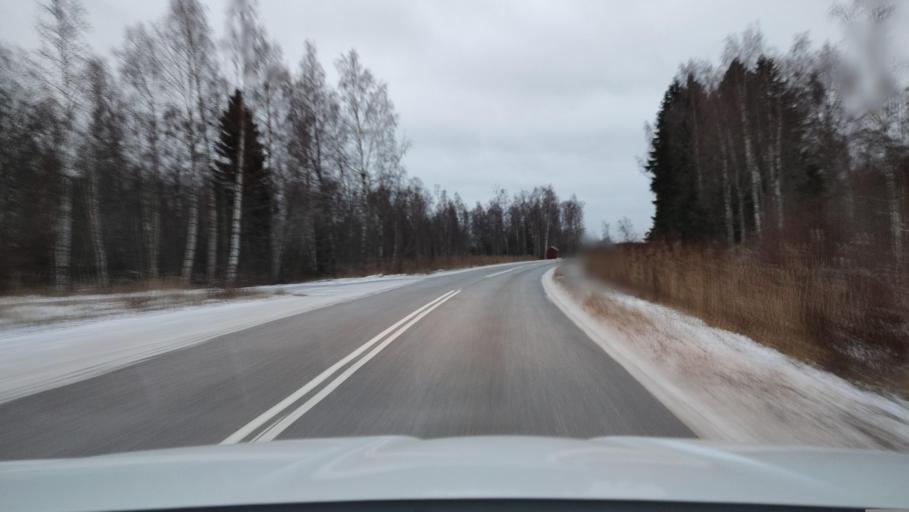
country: FI
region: Ostrobothnia
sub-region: Vaasa
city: Replot
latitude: 63.2807
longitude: 21.3399
